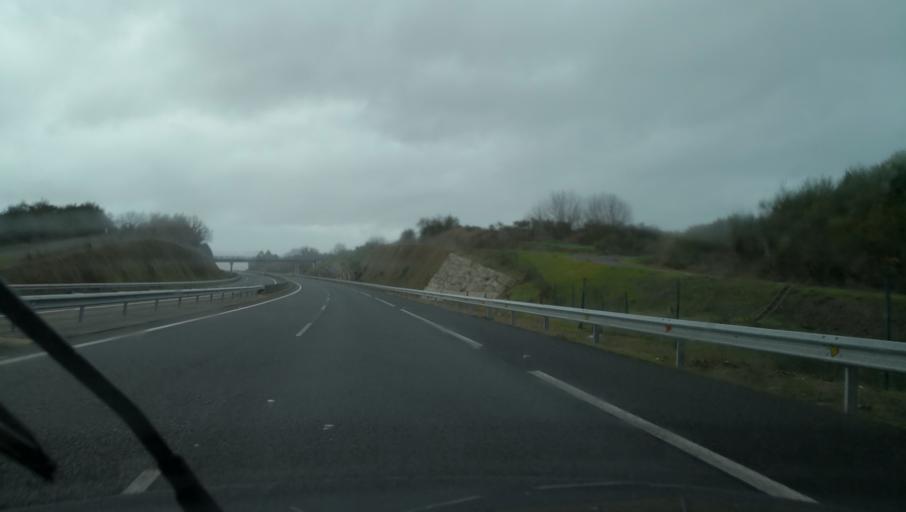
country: ES
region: Galicia
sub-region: Provincia de Pontevedra
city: Silleda
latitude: 42.6894
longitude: -8.1778
